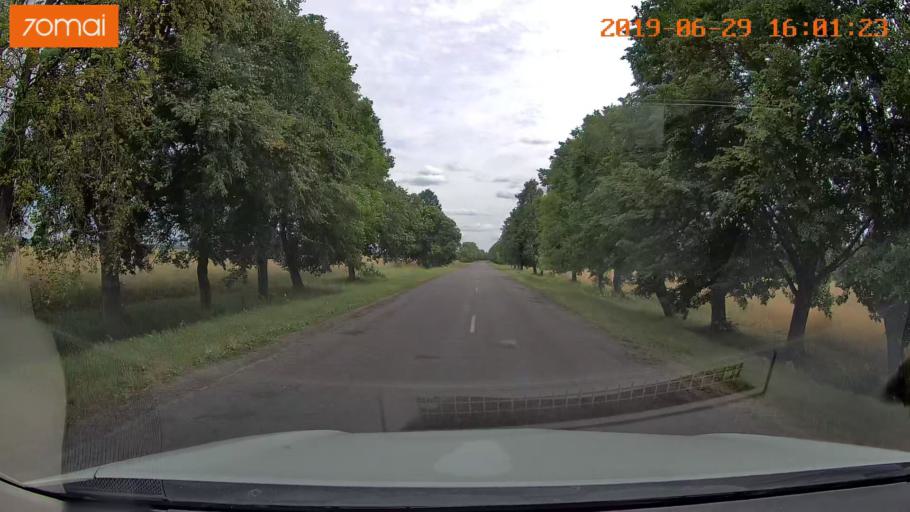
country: BY
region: Brest
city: Luninyets
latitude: 52.2481
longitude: 27.0166
